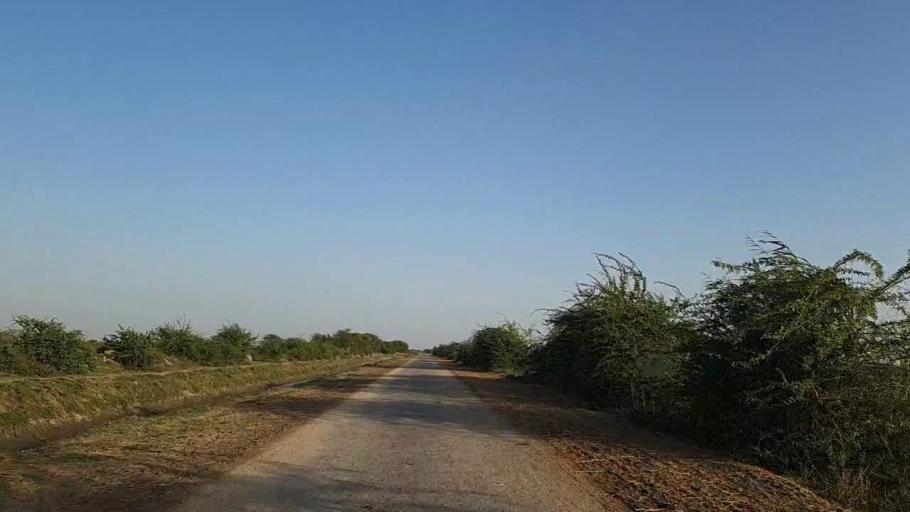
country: PK
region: Sindh
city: Jati
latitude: 24.4094
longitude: 68.3499
